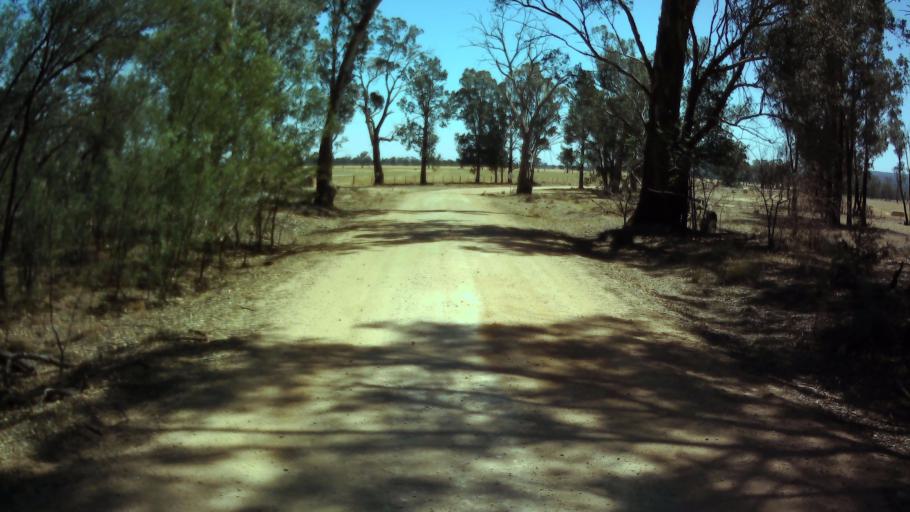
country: AU
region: New South Wales
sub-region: Weddin
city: Grenfell
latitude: -34.0275
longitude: 147.9619
